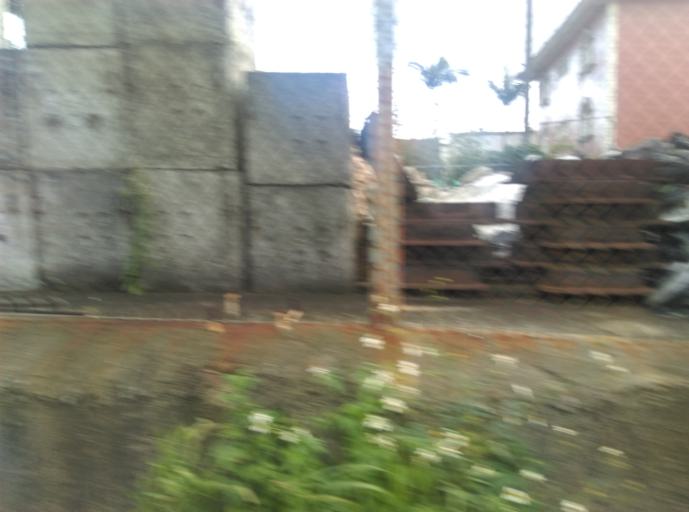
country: TW
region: Taiwan
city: Taoyuan City
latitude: 24.9935
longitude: 121.2524
